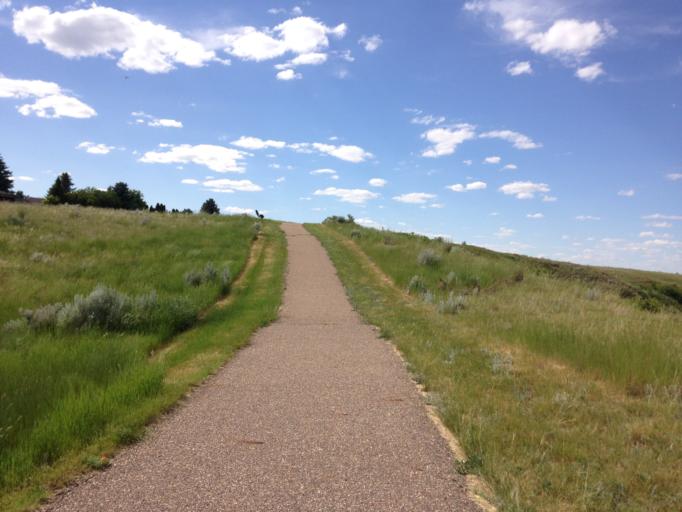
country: CA
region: Alberta
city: Medicine Hat
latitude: 50.0119
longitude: -110.6217
